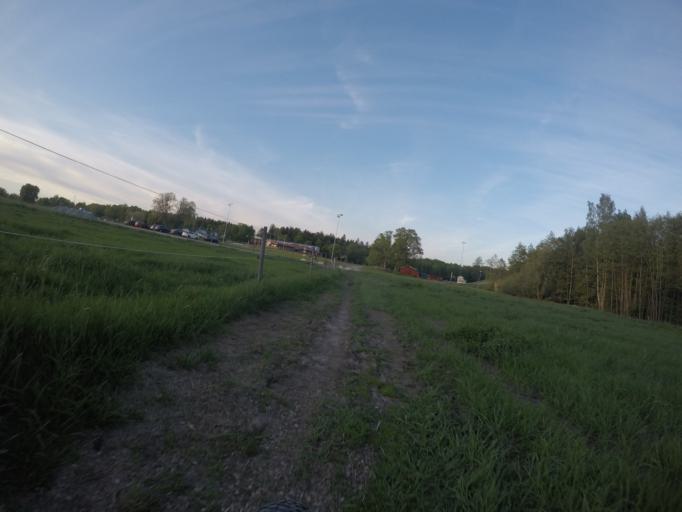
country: SE
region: Soedermanland
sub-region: Eskilstuna Kommun
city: Eskilstuna
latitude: 59.3485
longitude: 16.5079
